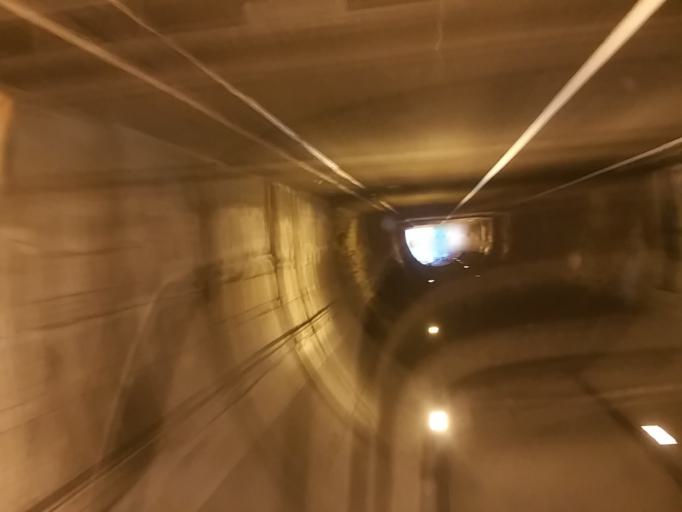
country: IT
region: Piedmont
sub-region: Provincia Verbano-Cusio-Ossola
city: Trasquera
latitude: 46.2064
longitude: 8.1971
